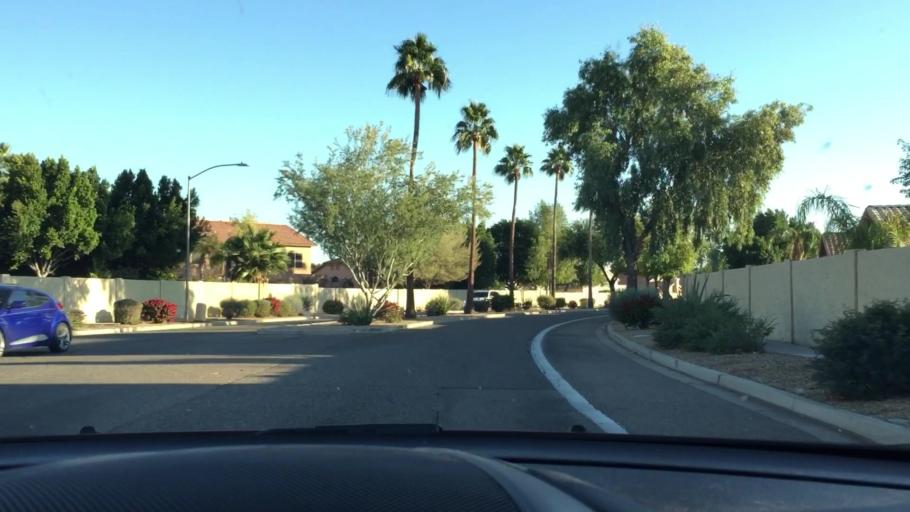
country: US
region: Arizona
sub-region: Maricopa County
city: Sun City
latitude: 33.6572
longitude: -112.2296
